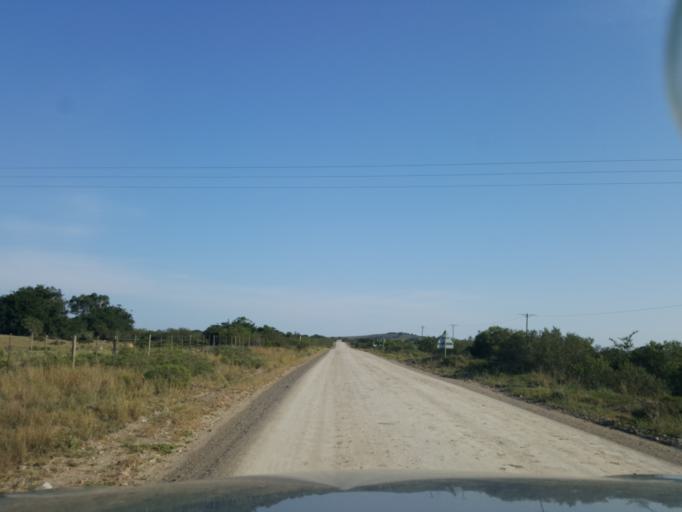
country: ZA
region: Eastern Cape
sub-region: Cacadu District Municipality
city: Grahamstown
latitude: -33.3811
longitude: 26.3009
